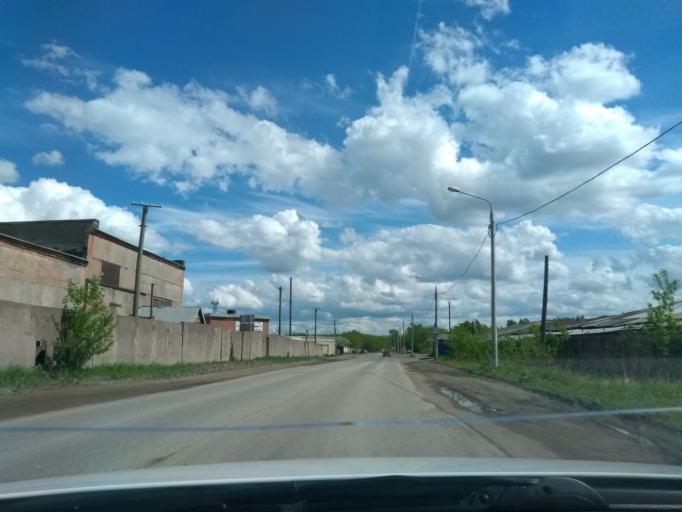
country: RU
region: Perm
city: Kondratovo
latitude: 58.0084
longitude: 56.1118
